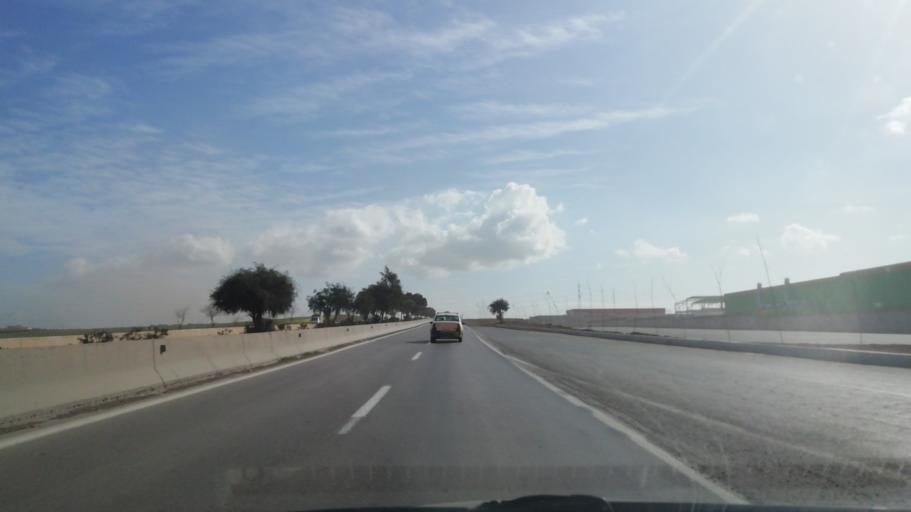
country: DZ
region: Oran
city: Ain el Bya
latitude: 35.7750
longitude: -0.2542
